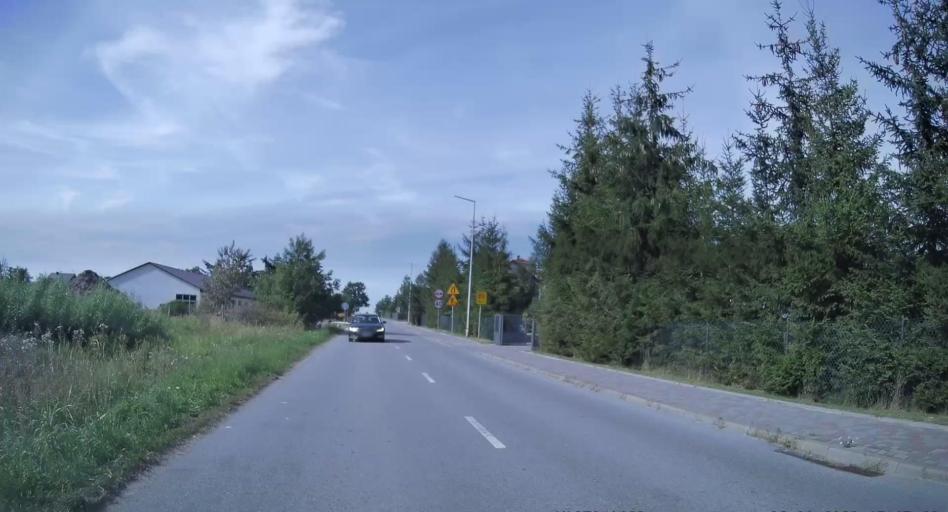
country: PL
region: Lodz Voivodeship
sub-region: Powiat opoczynski
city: Mniszkow
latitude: 51.3714
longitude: 20.0391
